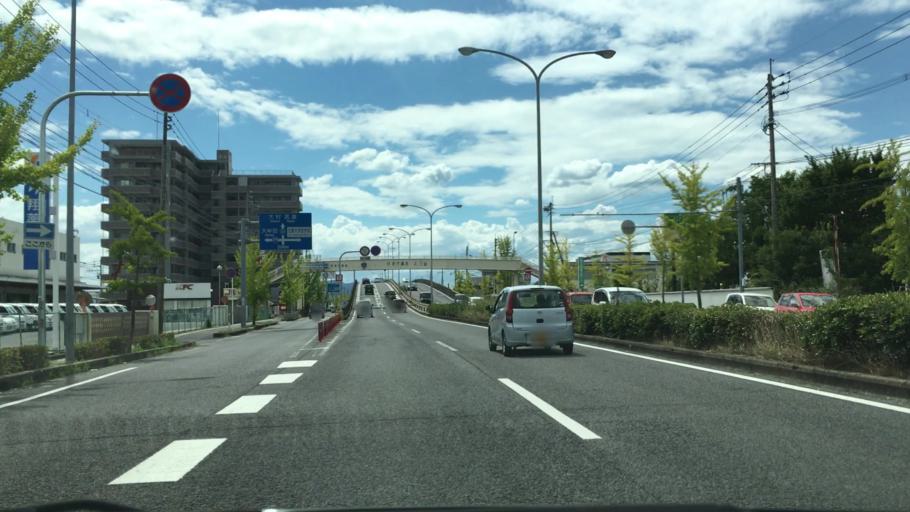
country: JP
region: Saga Prefecture
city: Saga-shi
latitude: 33.2723
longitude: 130.2740
